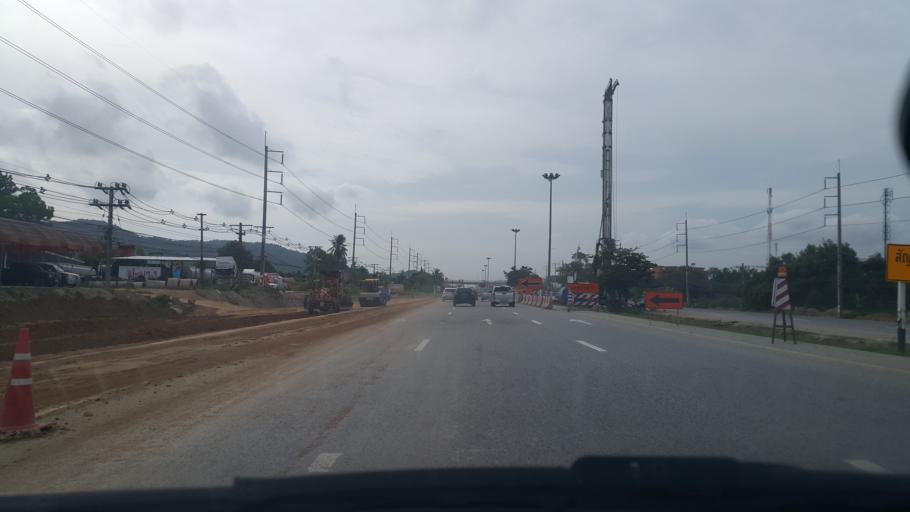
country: TH
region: Rayong
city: Nikhom Phattana
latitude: 12.8094
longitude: 101.1422
